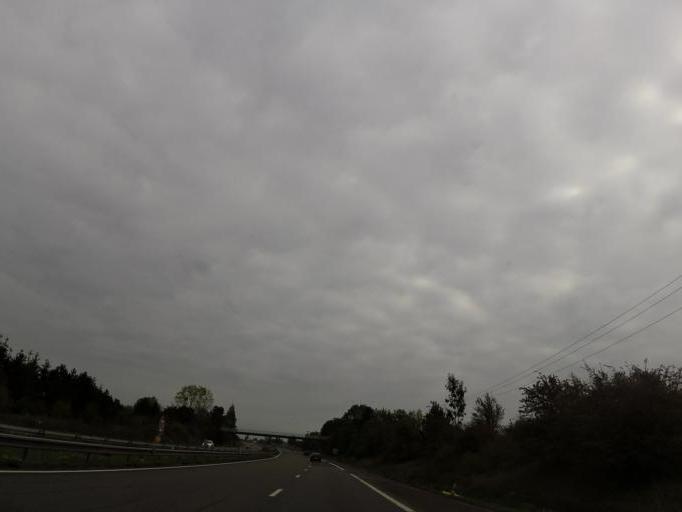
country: FR
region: Lorraine
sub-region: Departement de la Moselle
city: Retonfey
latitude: 49.1264
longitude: 6.2972
